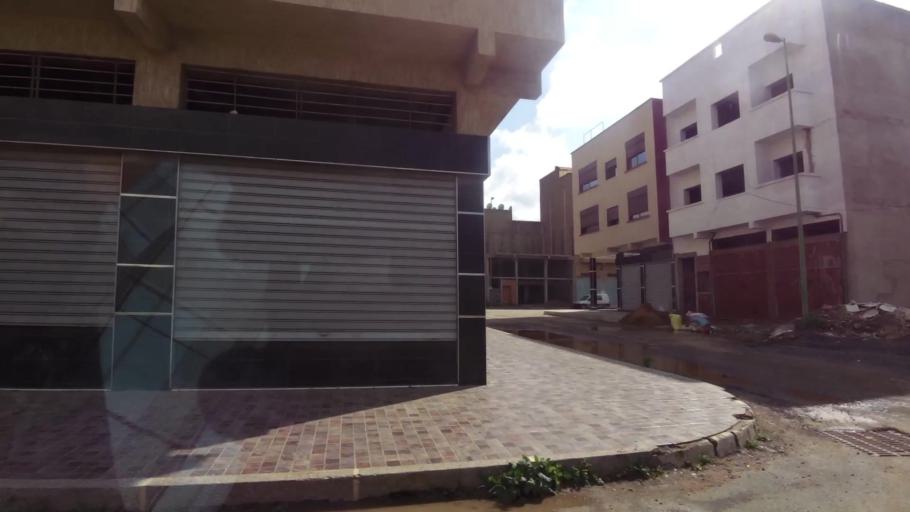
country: MA
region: Chaouia-Ouardigha
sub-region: Settat Province
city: Berrechid
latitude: 33.2634
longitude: -7.5699
